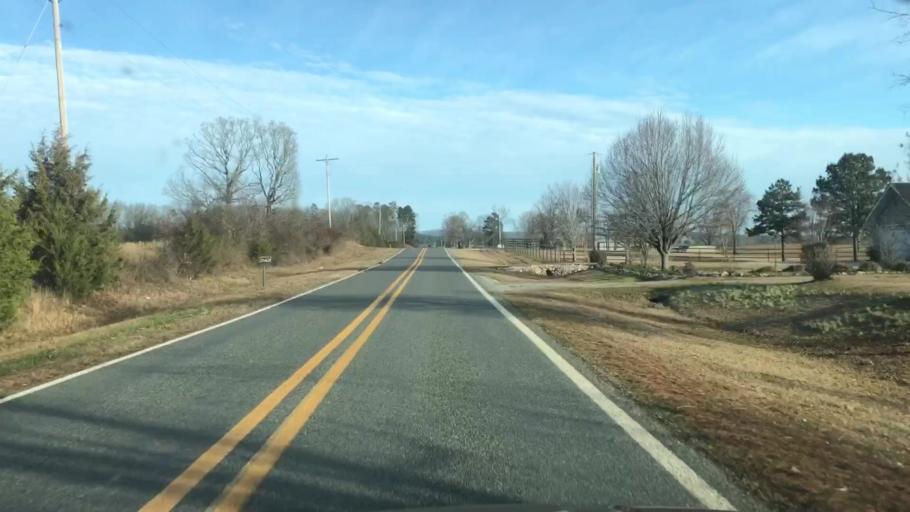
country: US
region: Arkansas
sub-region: Garland County
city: Rockwell
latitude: 34.4988
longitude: -93.2764
